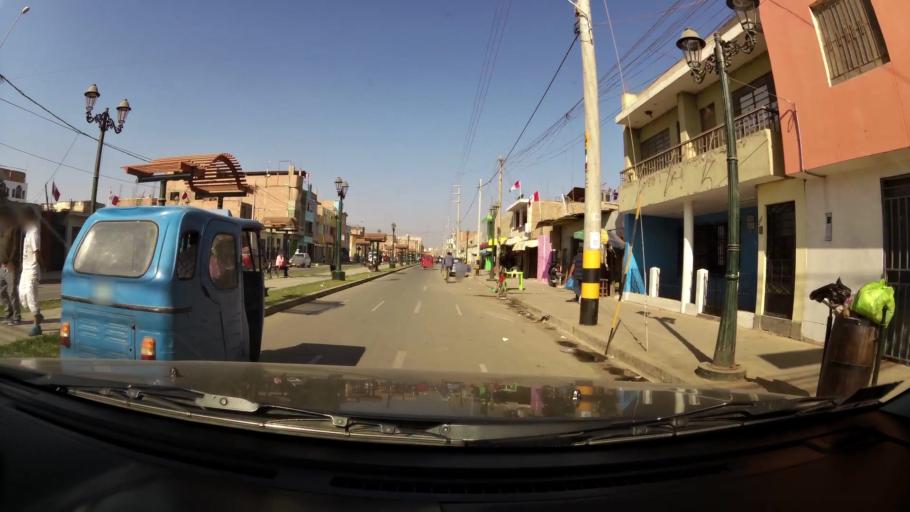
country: PE
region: Ica
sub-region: Provincia de Chincha
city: Chincha Alta
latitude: -13.4155
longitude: -76.1384
